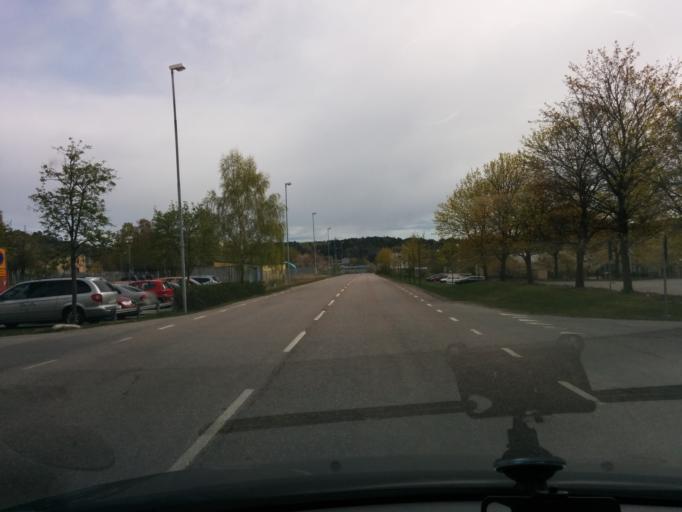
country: SE
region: Stockholm
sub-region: Botkyrka Kommun
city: Alby
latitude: 59.2387
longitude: 17.8538
